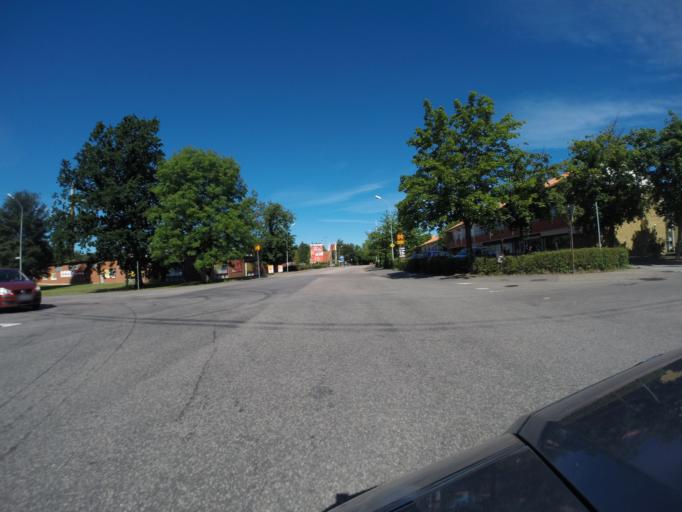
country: SE
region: Skane
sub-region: Bjuvs Kommun
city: Bjuv
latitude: 56.0824
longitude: 12.9222
